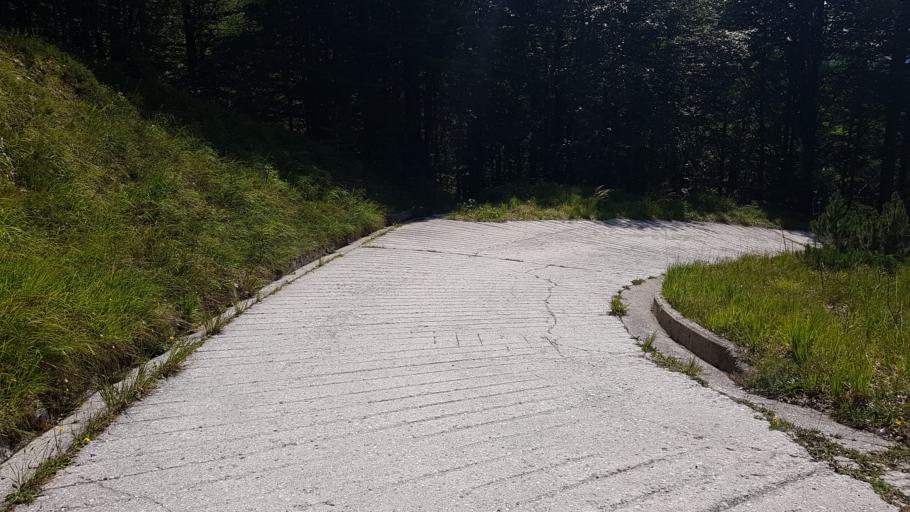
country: IT
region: Friuli Venezia Giulia
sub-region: Provincia di Udine
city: Moggio Udinese
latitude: 46.4691
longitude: 13.2340
